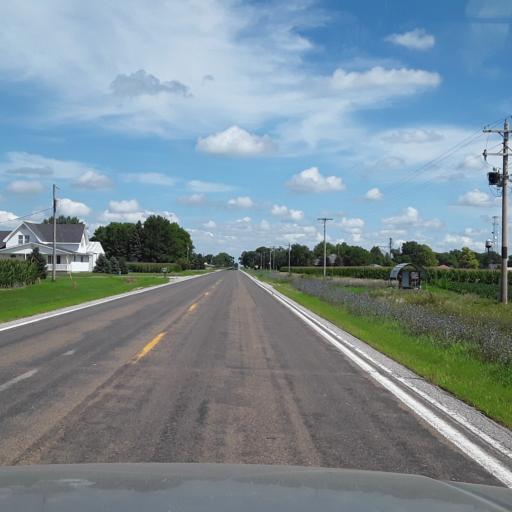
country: US
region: Nebraska
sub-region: Polk County
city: Osceola
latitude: 41.0204
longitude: -97.4062
